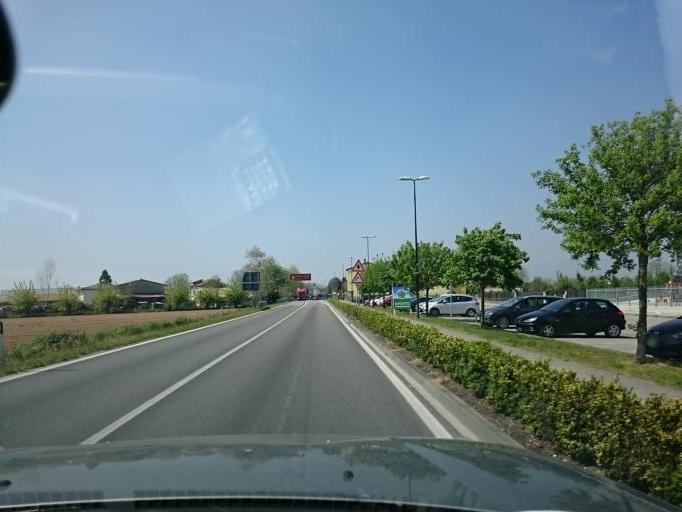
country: IT
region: Veneto
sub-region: Provincia di Vicenza
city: Rossano Veneto
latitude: 45.7009
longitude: 11.8226
